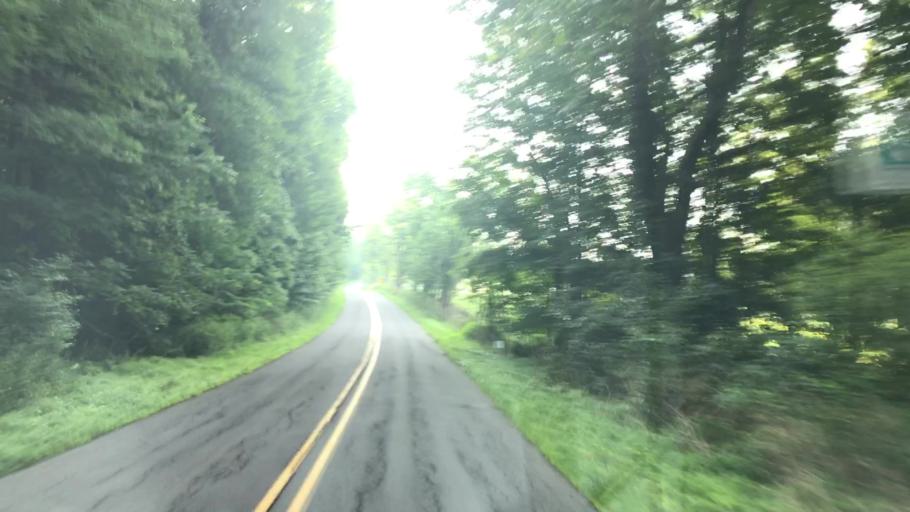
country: US
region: Pennsylvania
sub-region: Wyoming County
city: Factoryville
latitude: 41.6105
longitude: -75.7371
